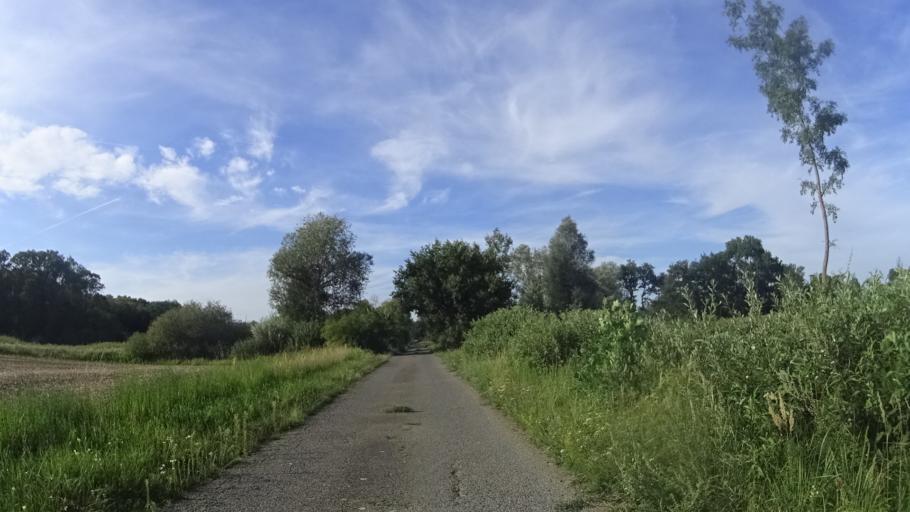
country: AT
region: Lower Austria
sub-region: Politischer Bezirk Ganserndorf
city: Drosing
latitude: 48.5747
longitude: 16.9536
